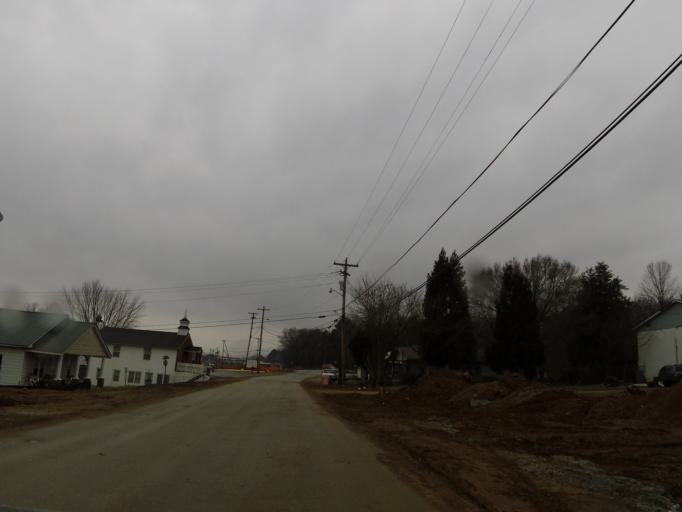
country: US
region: Tennessee
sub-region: Roane County
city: Harriman
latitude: 35.9198
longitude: -84.5637
